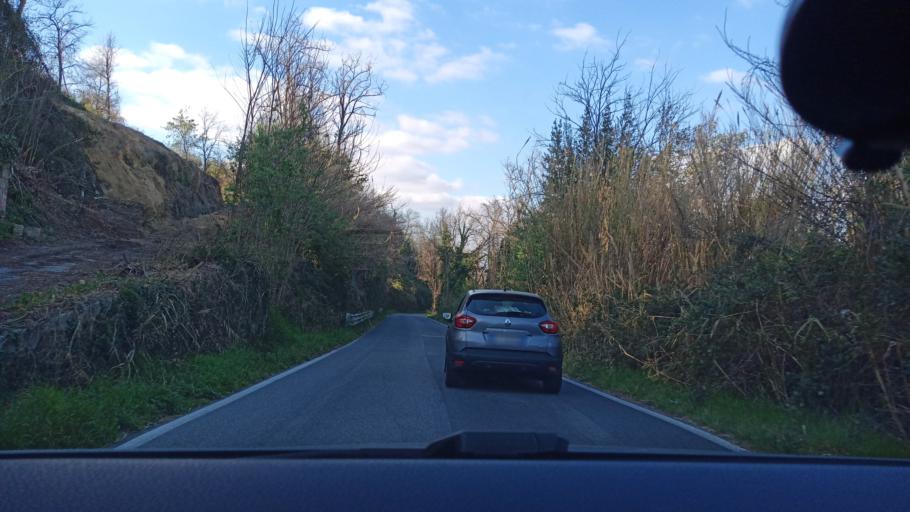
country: IT
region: Latium
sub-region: Citta metropolitana di Roma Capitale
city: Torrita Tiberina
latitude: 42.2450
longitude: 12.6190
